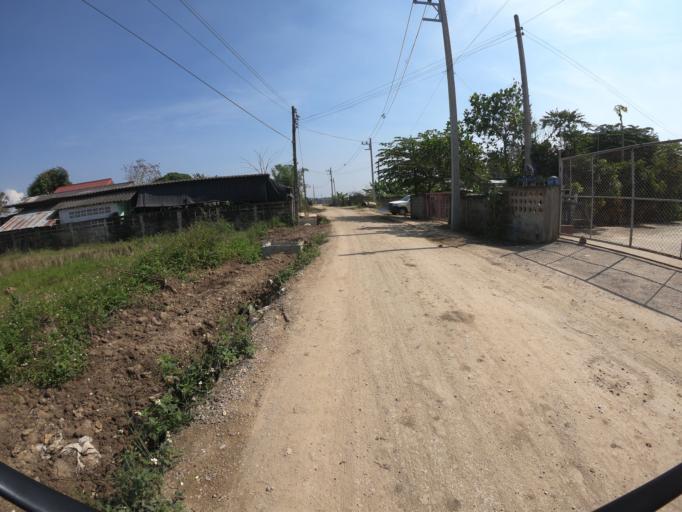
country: TH
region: Chiang Mai
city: San Sai
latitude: 18.8706
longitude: 98.9877
